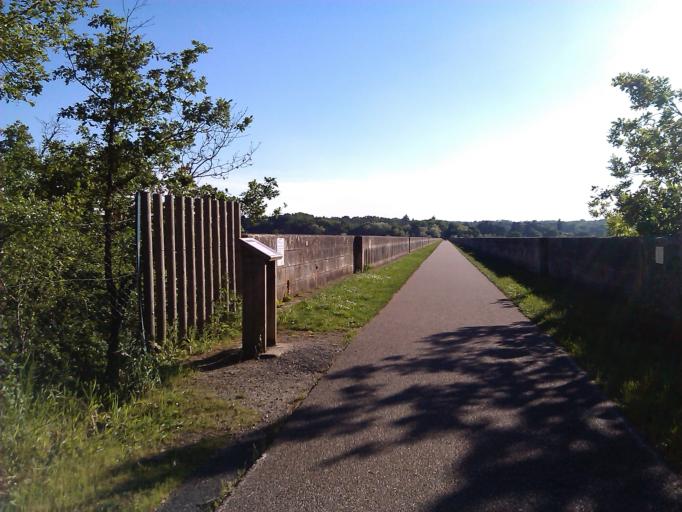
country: FR
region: Centre
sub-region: Departement de l'Indre
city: Le Blanc
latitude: 46.6418
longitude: 1.0572
